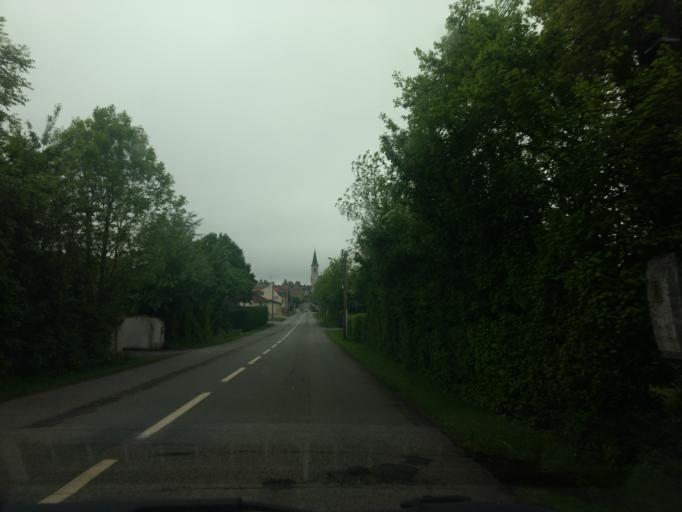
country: FR
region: Midi-Pyrenees
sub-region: Departement de l'Aveyron
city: Montbazens
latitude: 44.4504
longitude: 2.2528
